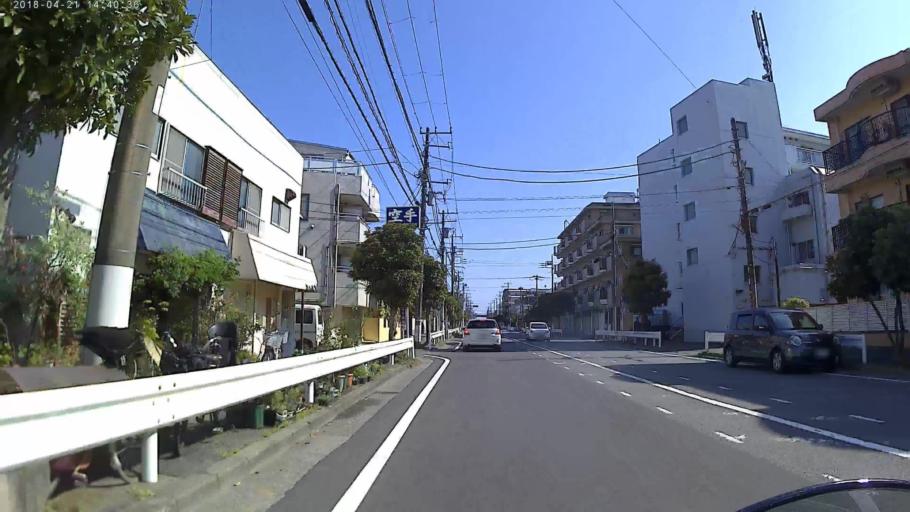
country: JP
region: Kanagawa
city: Hiratsuka
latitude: 35.3223
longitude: 139.3468
